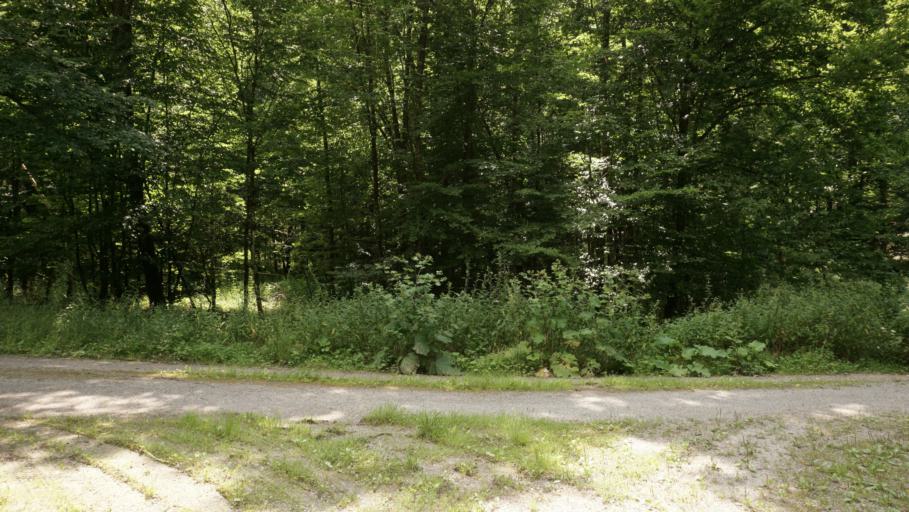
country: DE
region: Baden-Wuerttemberg
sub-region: Karlsruhe Region
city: Hassmersheim
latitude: 49.3226
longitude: 9.1790
